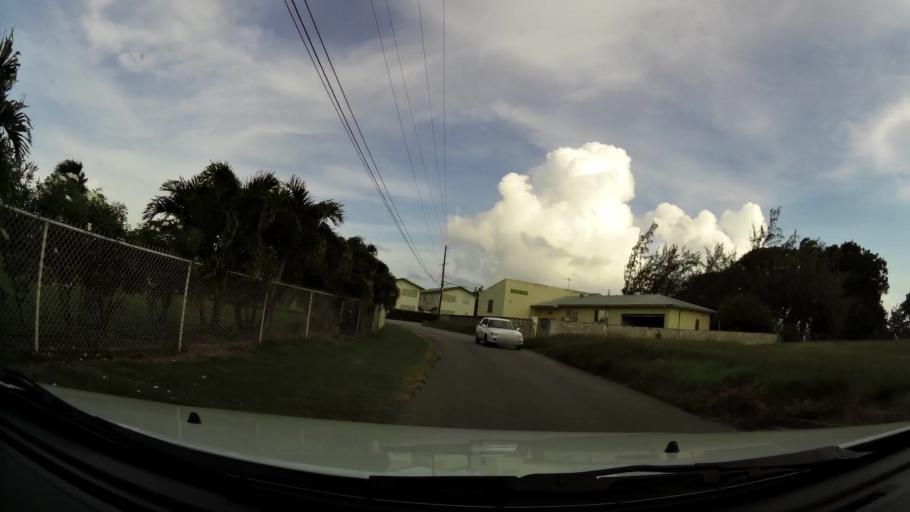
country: BB
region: Christ Church
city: Oistins
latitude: 13.0690
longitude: -59.5341
